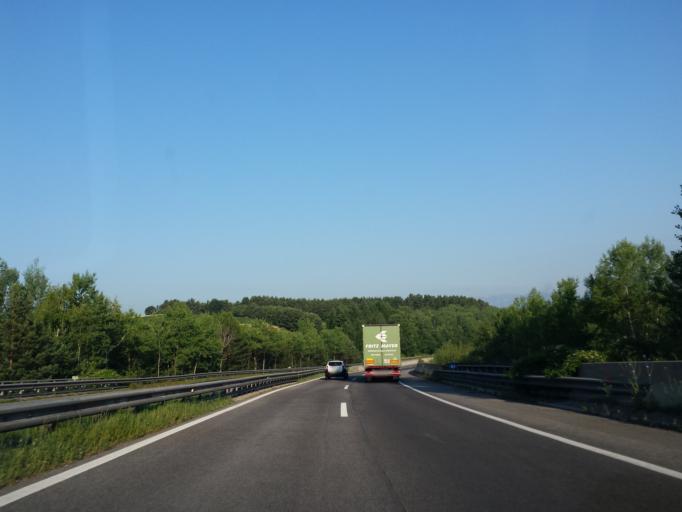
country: AT
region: Lower Austria
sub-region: Politischer Bezirk Neunkirchen
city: Altendorf
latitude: 47.6722
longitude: 16.0005
